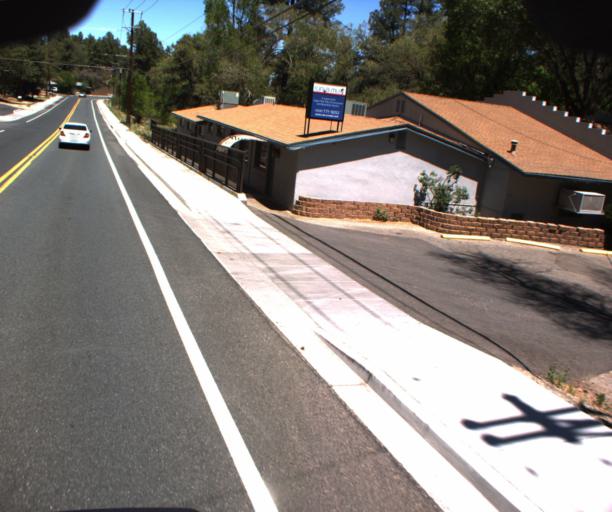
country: US
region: Arizona
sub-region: Yavapai County
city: Prescott
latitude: 34.5214
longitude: -112.4796
